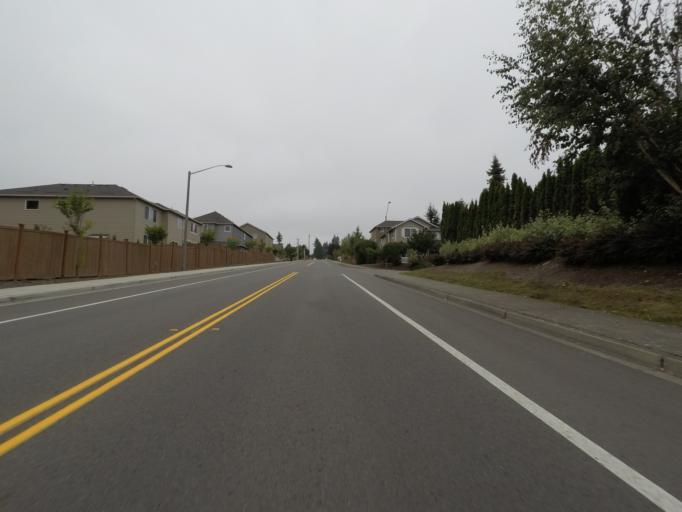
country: US
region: Washington
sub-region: King County
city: Kenmore
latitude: 47.7749
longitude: -122.2275
